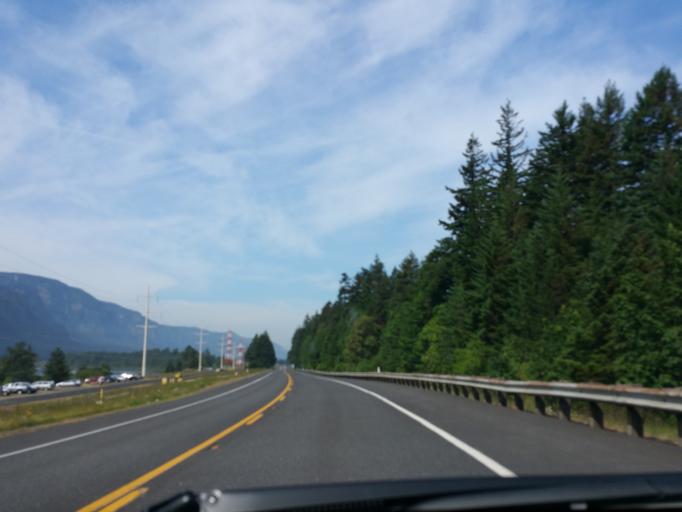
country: US
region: Oregon
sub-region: Hood River County
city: Cascade Locks
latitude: 45.6517
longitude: -121.9438
